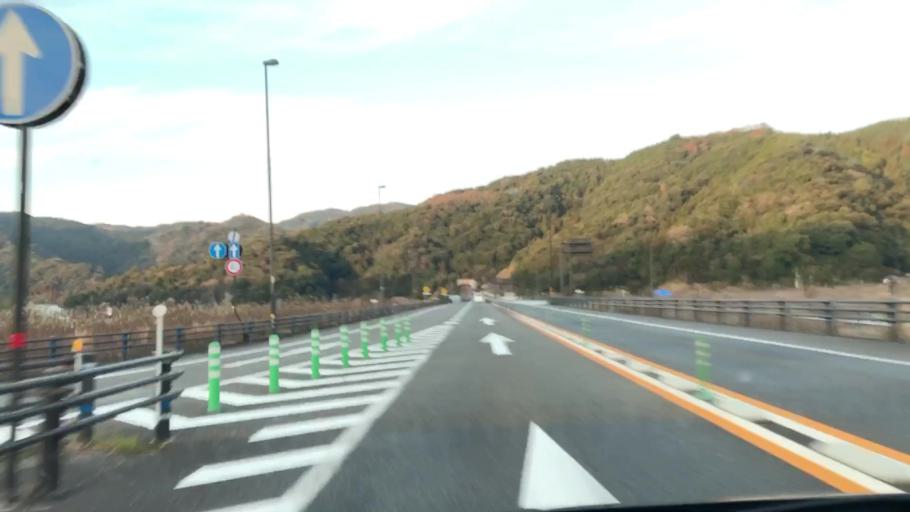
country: JP
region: Kumamoto
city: Minamata
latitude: 32.2982
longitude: 130.5091
